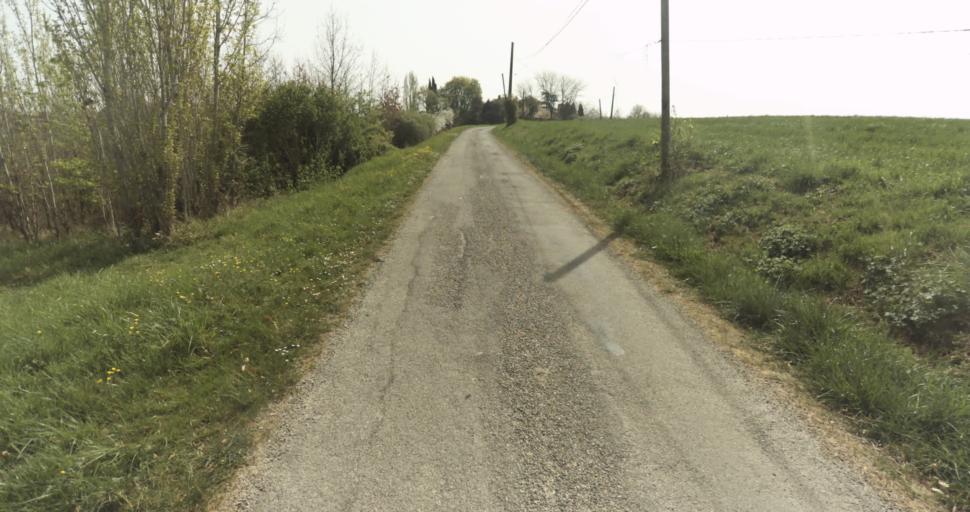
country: FR
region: Midi-Pyrenees
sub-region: Departement du Tarn-et-Garonne
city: Moissac
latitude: 44.1144
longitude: 1.0649
